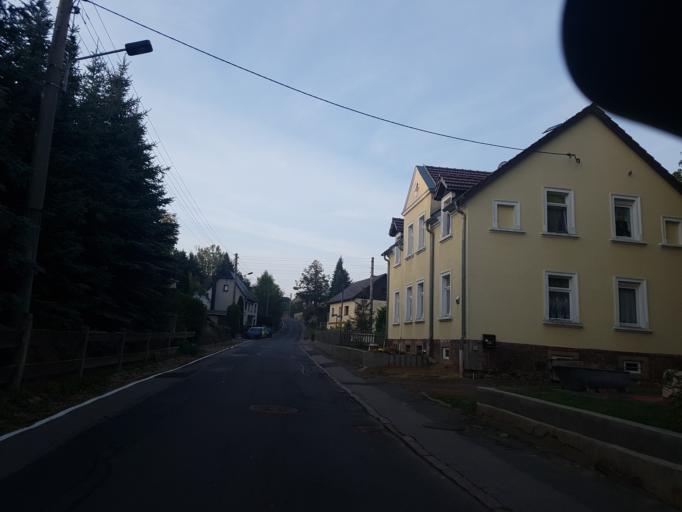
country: DE
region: Saxony
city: Waldheim
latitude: 51.1050
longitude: 13.0573
